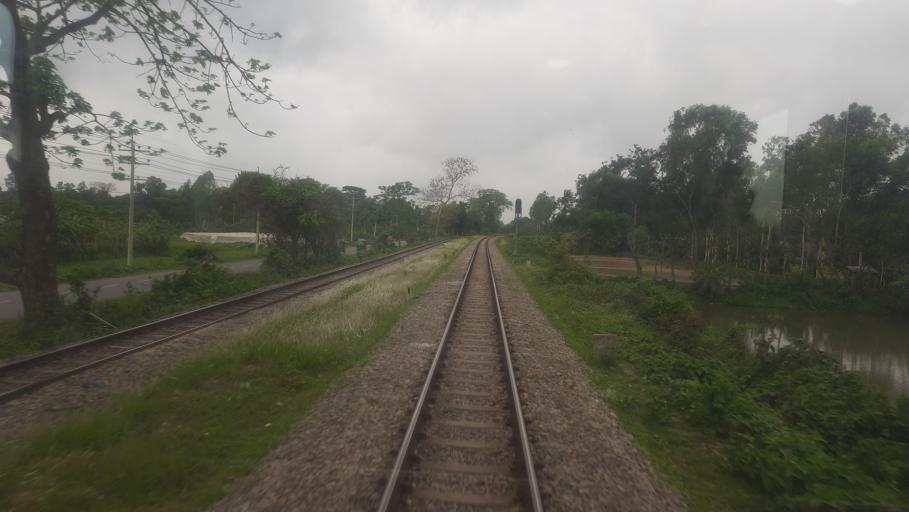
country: BD
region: Dhaka
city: Narsingdi
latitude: 23.9330
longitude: 90.7608
